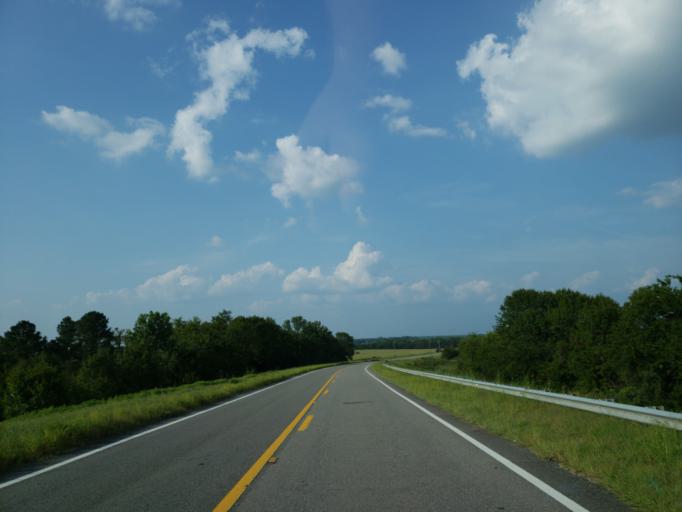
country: US
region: Alabama
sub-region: Greene County
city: Eutaw
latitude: 32.7882
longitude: -87.9751
